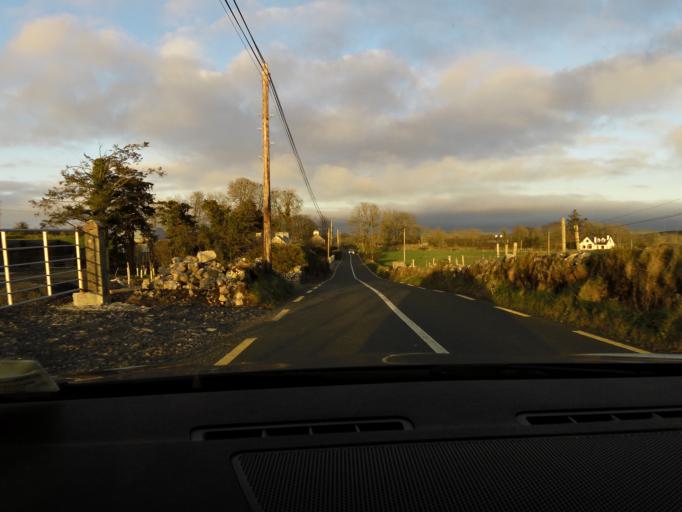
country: IE
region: Connaught
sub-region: Sligo
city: Tobercurry
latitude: 54.0436
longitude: -8.6476
